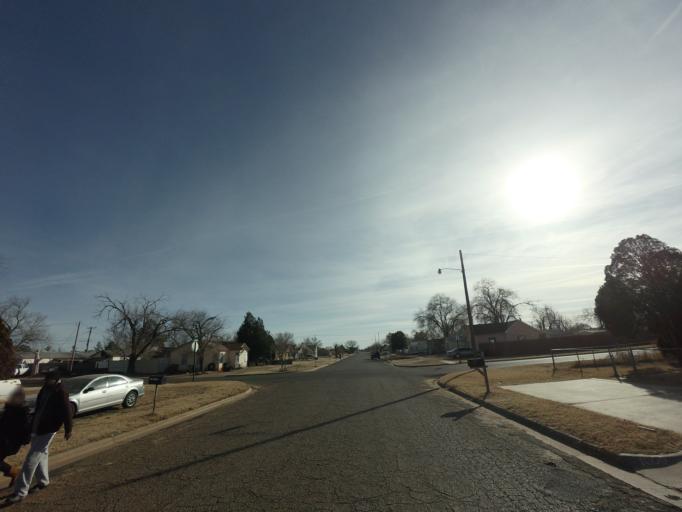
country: US
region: New Mexico
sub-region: Curry County
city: Clovis
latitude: 34.4081
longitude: -103.2180
